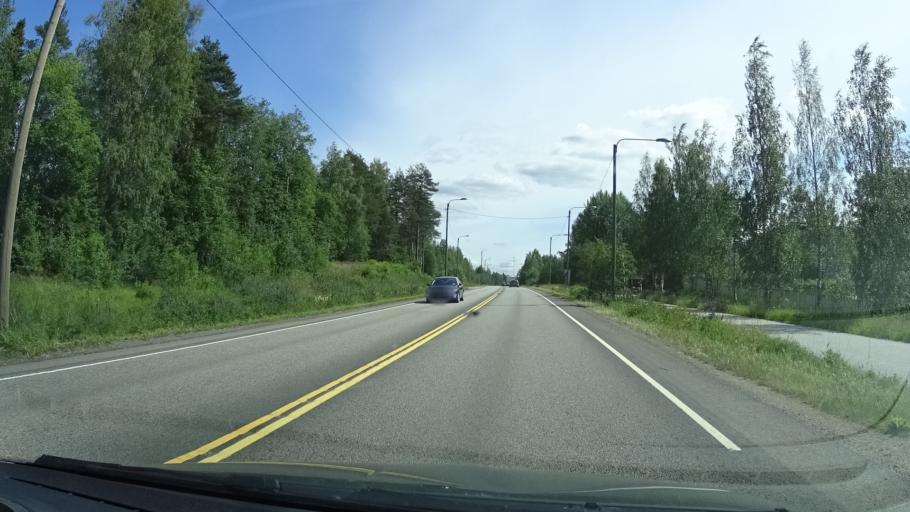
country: FI
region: Central Finland
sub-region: Jyvaeskylae
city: Uurainen
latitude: 62.2659
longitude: 25.4478
